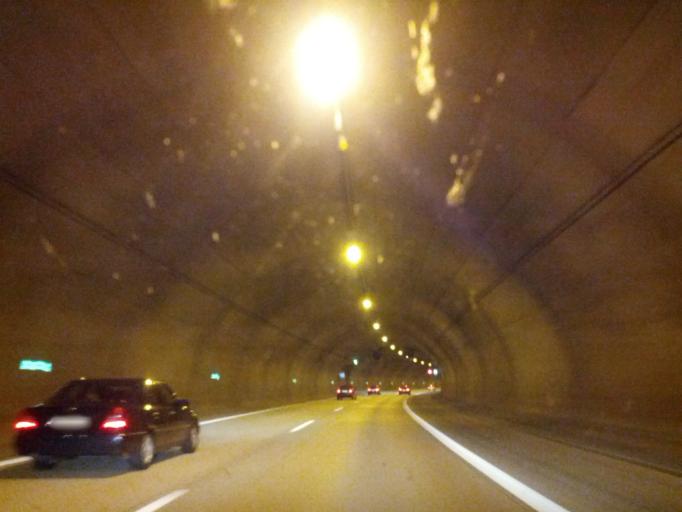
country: DE
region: Saxony
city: Freital
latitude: 51.0272
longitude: 13.6795
